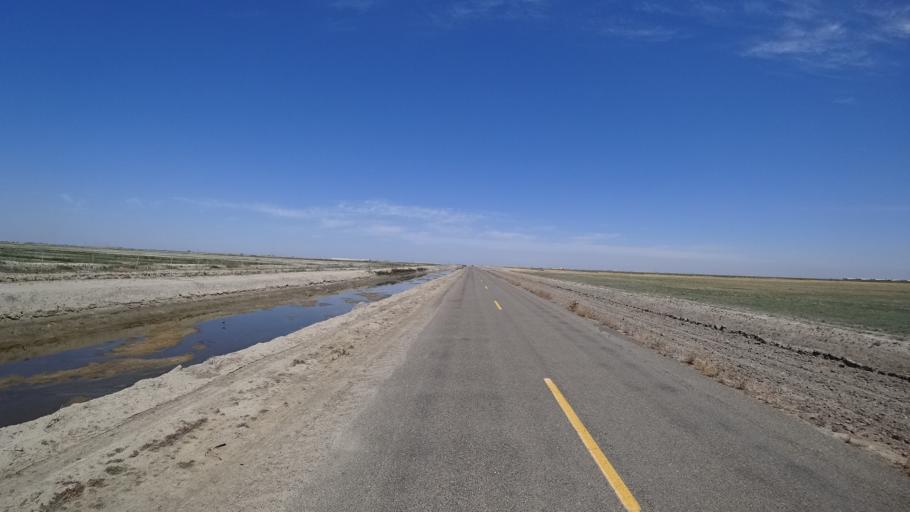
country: US
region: California
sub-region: Kings County
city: Corcoran
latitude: 36.1289
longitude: -119.6802
